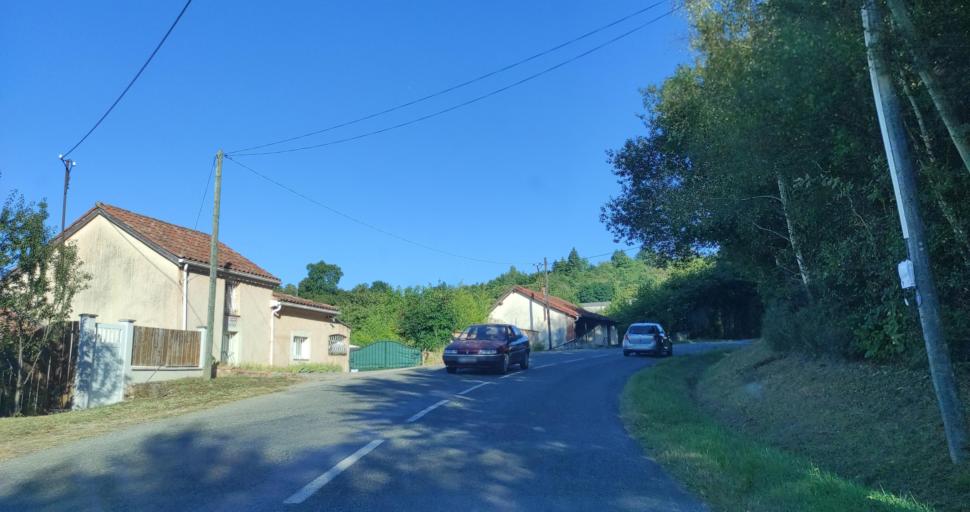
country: FR
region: Midi-Pyrenees
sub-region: Departement de l'Aveyron
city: Firmi
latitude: 44.5212
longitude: 2.3050
